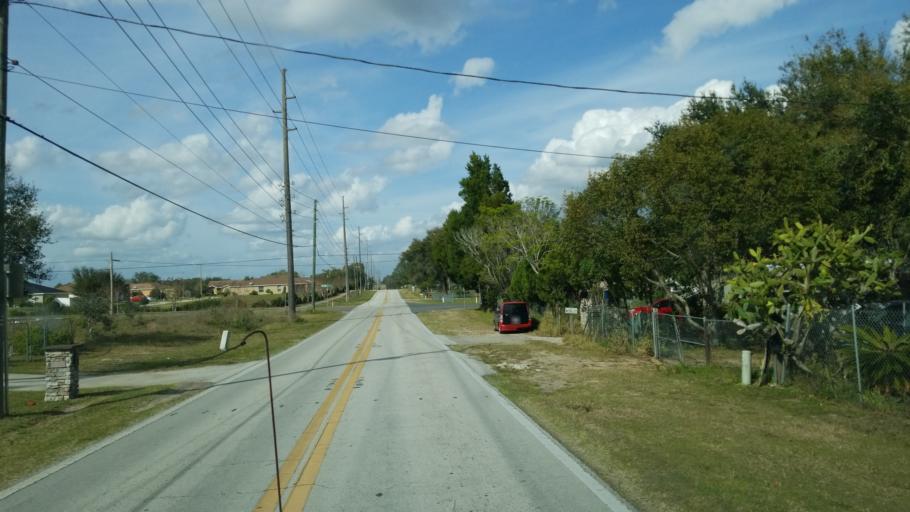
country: US
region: Florida
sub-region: Polk County
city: Davenport
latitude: 28.1459
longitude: -81.5903
